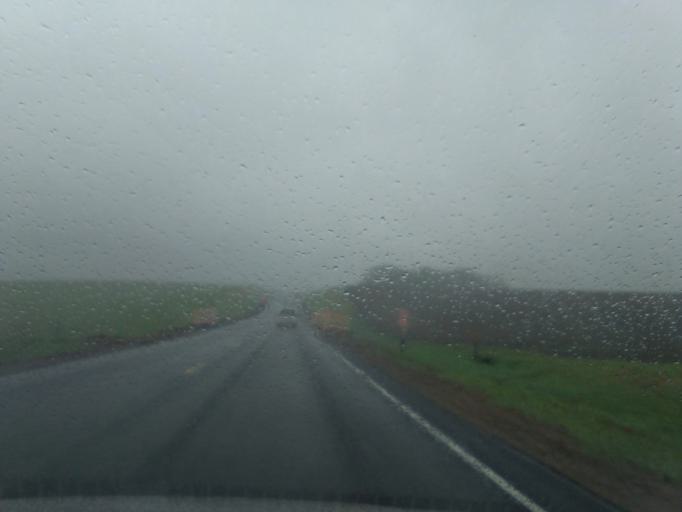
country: US
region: Nebraska
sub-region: Wayne County
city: Wayne
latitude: 42.1889
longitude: -97.1761
